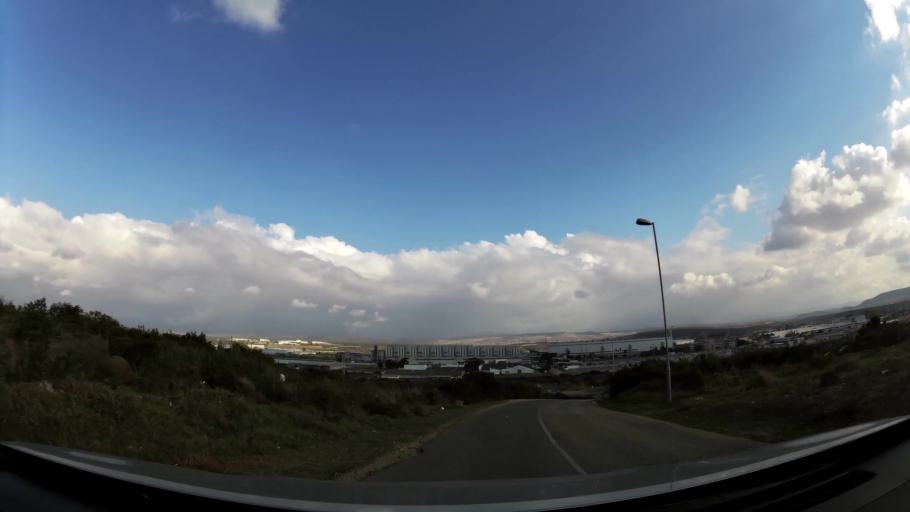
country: ZA
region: Eastern Cape
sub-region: Nelson Mandela Bay Metropolitan Municipality
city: Uitenhage
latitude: -33.7793
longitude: 25.4251
